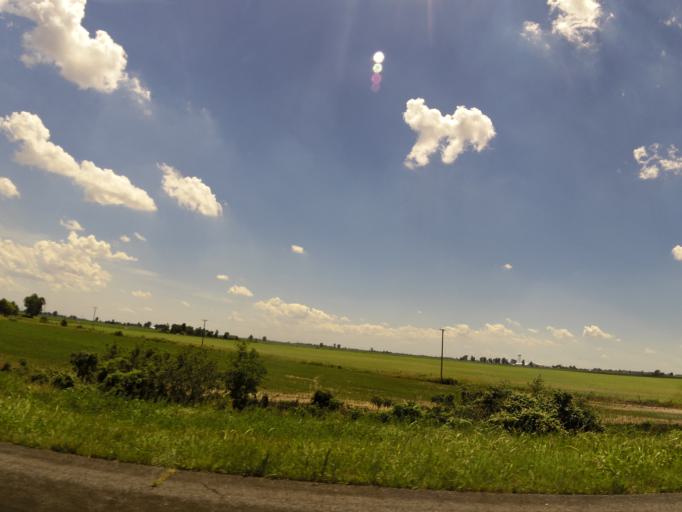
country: US
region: Missouri
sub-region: Pemiscot County
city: Caruthersville
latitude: 36.1815
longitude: -89.6989
